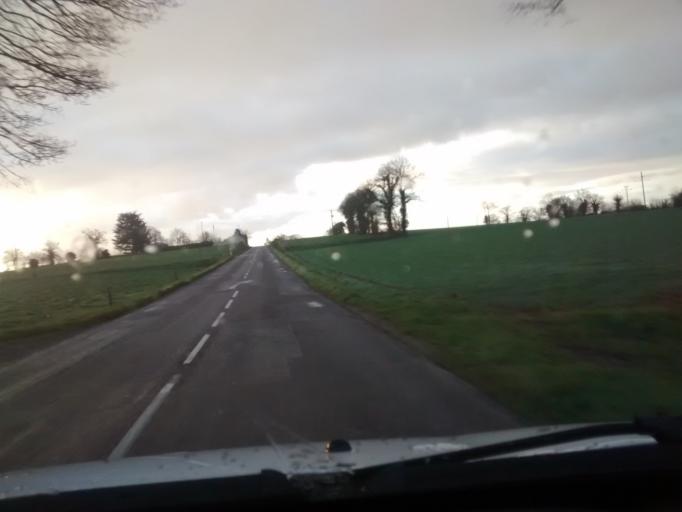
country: FR
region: Brittany
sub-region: Departement d'Ille-et-Vilaine
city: Domalain
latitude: 47.9722
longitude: -1.2685
